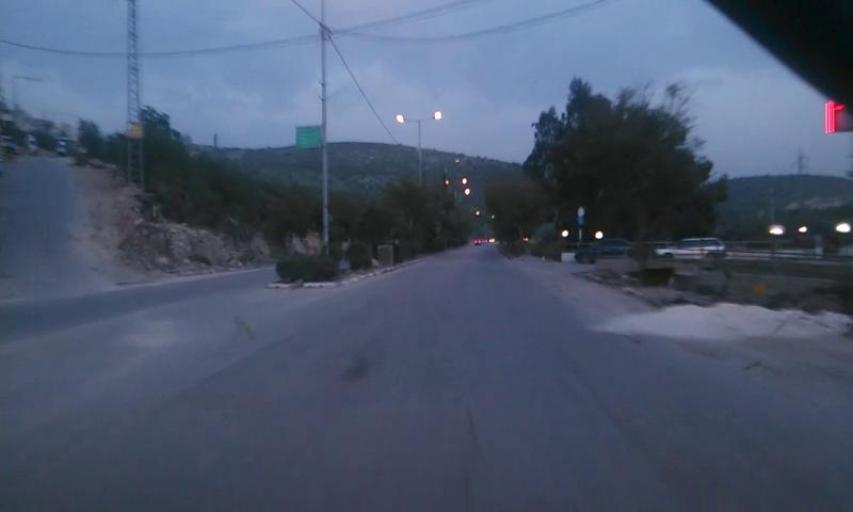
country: PS
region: West Bank
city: `Anabta
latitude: 32.3032
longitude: 35.1286
